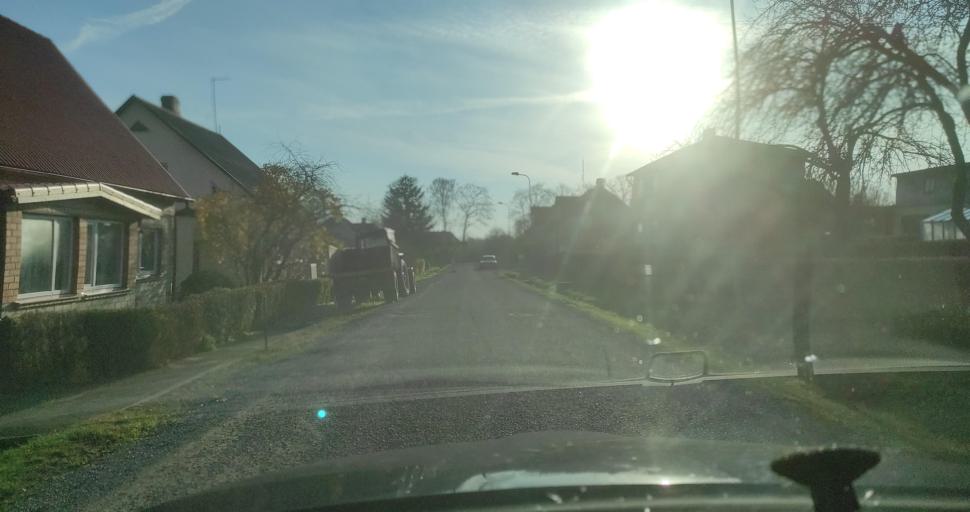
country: LV
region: Saldus Rajons
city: Saldus
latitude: 56.6739
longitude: 22.4999
